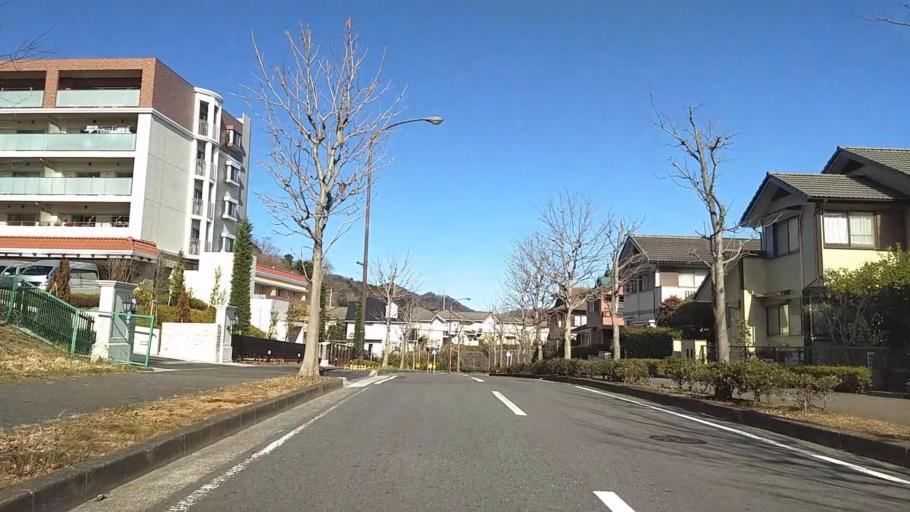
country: JP
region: Kanagawa
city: Atsugi
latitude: 35.4509
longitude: 139.3037
